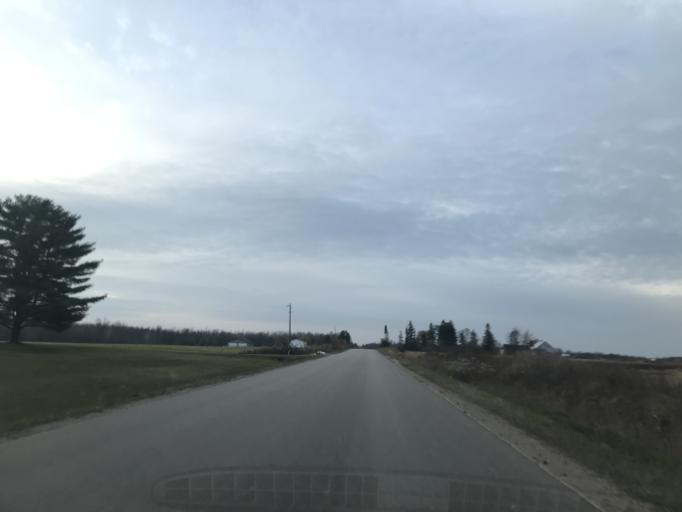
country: US
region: Wisconsin
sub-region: Marinette County
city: Peshtigo
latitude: 45.0817
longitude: -87.7996
